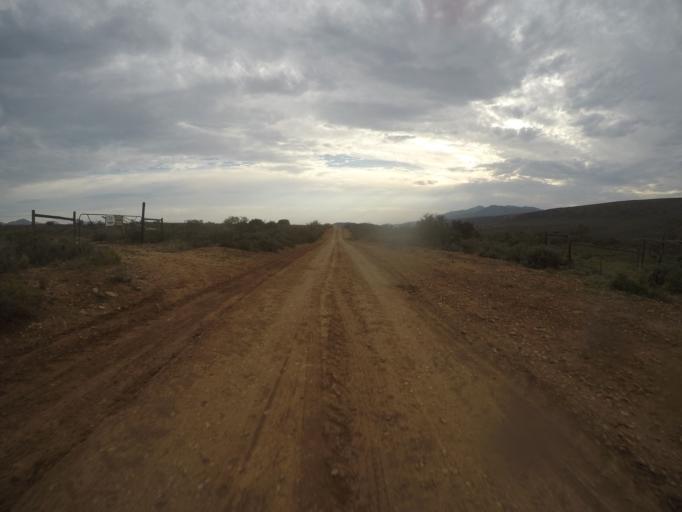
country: ZA
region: Eastern Cape
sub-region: Cacadu District Municipality
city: Willowmore
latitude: -33.4917
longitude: 23.5915
